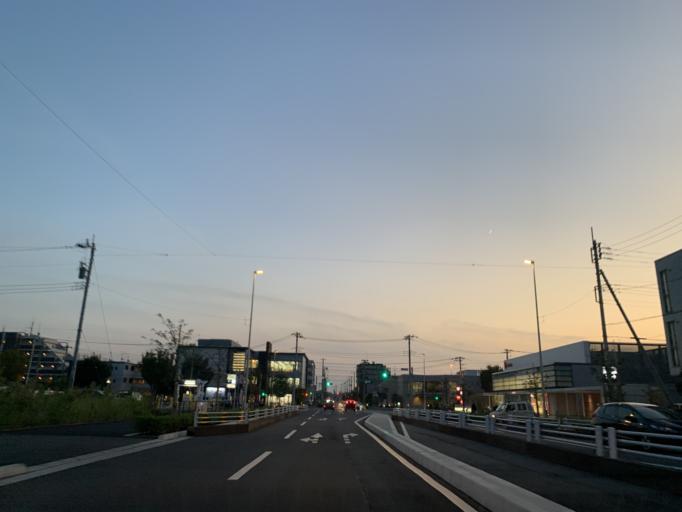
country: JP
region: Chiba
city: Nagareyama
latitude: 35.8714
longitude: 139.9232
